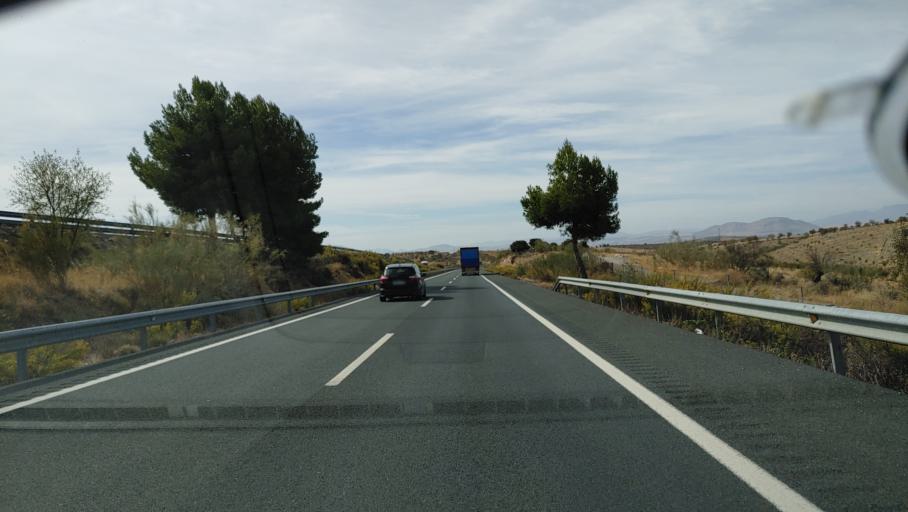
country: ES
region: Andalusia
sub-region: Provincia de Granada
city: Gor
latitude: 37.3941
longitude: -2.9675
